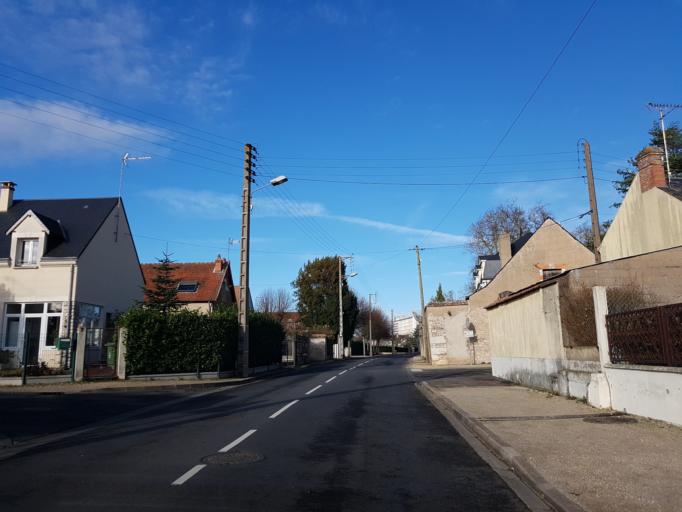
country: FR
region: Centre
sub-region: Departement du Loiret
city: Saint-Jean-le-Blanc
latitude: 47.8857
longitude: 1.9236
